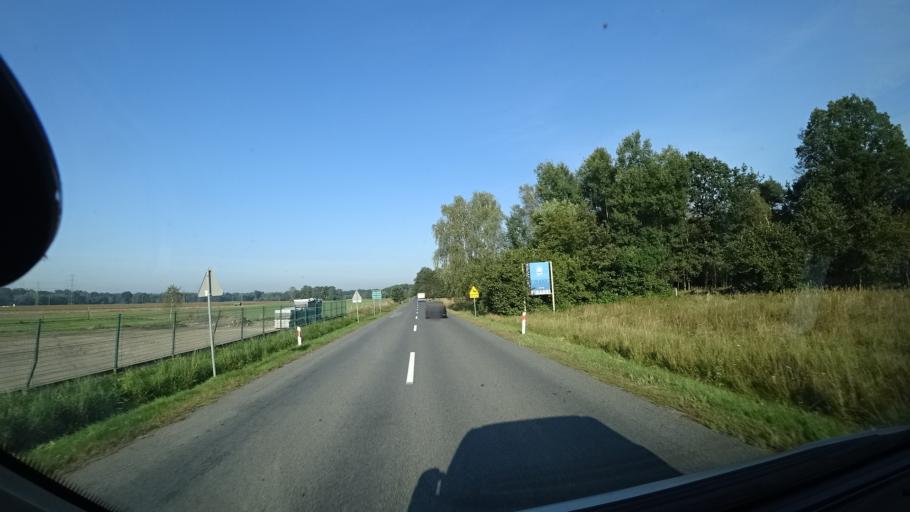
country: PL
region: Silesian Voivodeship
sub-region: Powiat gliwicki
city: Rudziniec
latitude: 50.2693
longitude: 18.4110
